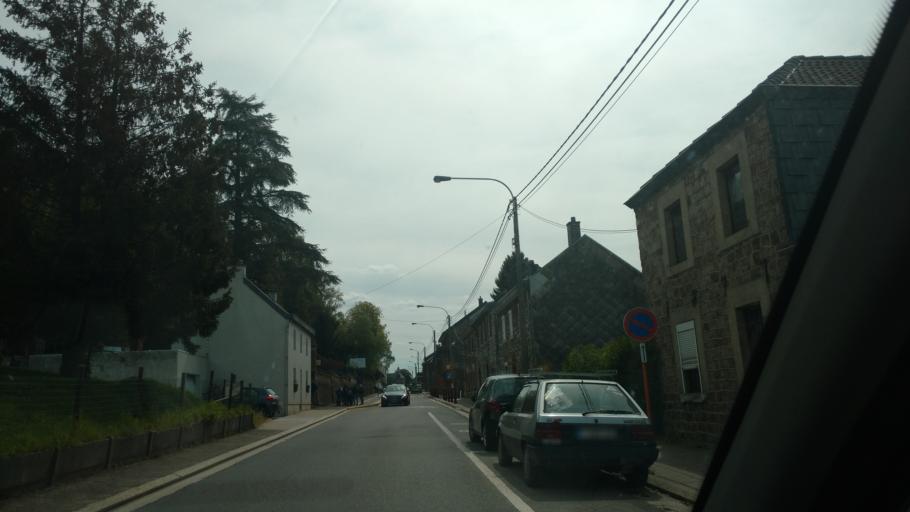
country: BE
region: Wallonia
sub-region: Province de Liege
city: La Calamine
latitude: 50.7359
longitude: 5.9890
